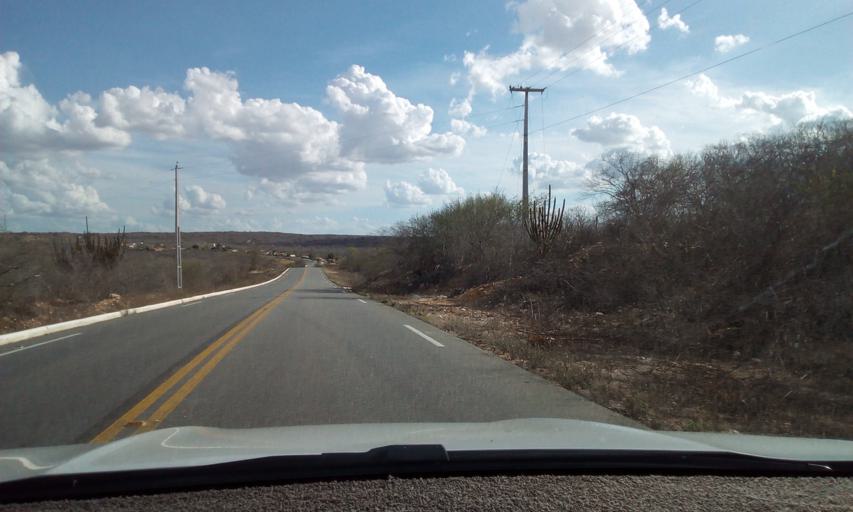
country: BR
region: Paraiba
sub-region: Soledade
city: Soledade
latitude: -6.8498
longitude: -36.4078
